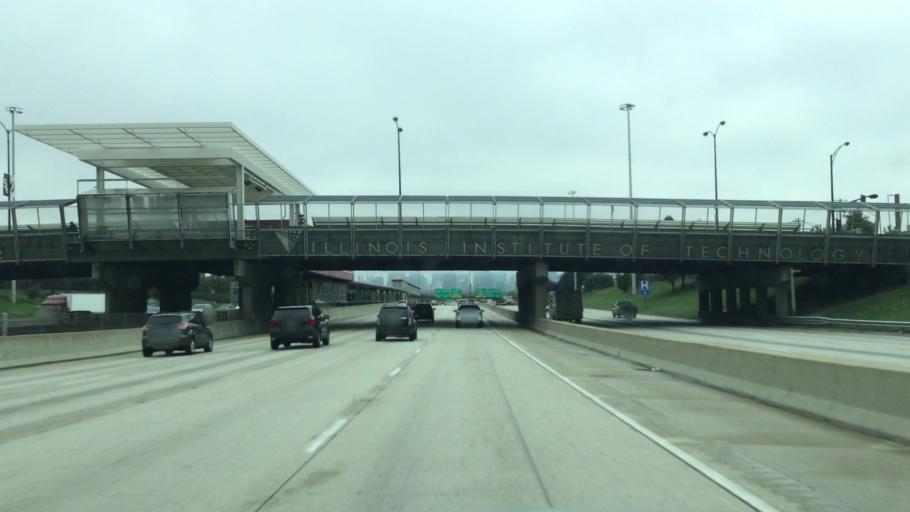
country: US
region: Illinois
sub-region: Cook County
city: Chicago
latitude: 41.8303
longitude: -87.6304
